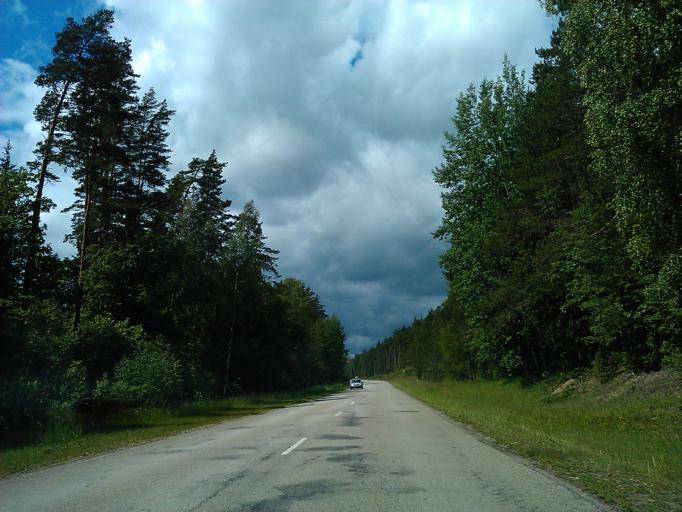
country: LV
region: Talsu Rajons
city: Stende
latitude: 57.0865
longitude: 22.5154
